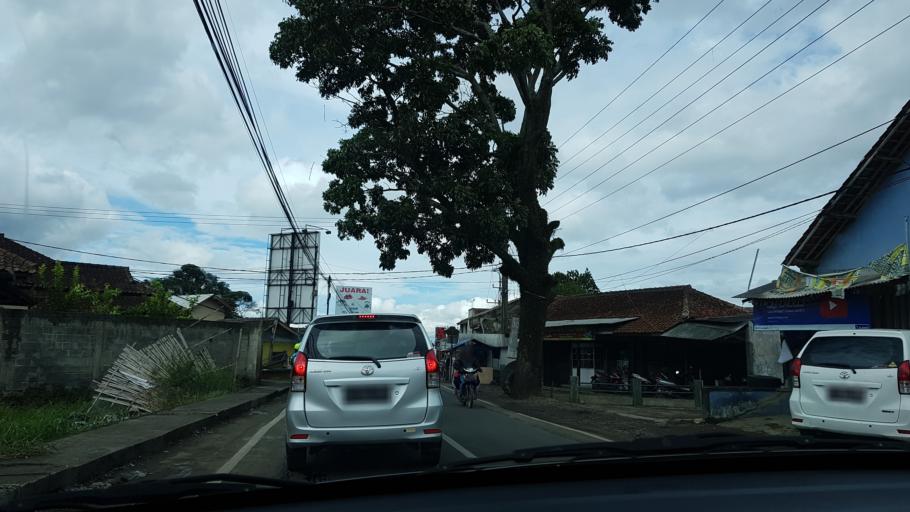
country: ID
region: West Java
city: Banjar
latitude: -7.1054
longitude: 107.4575
